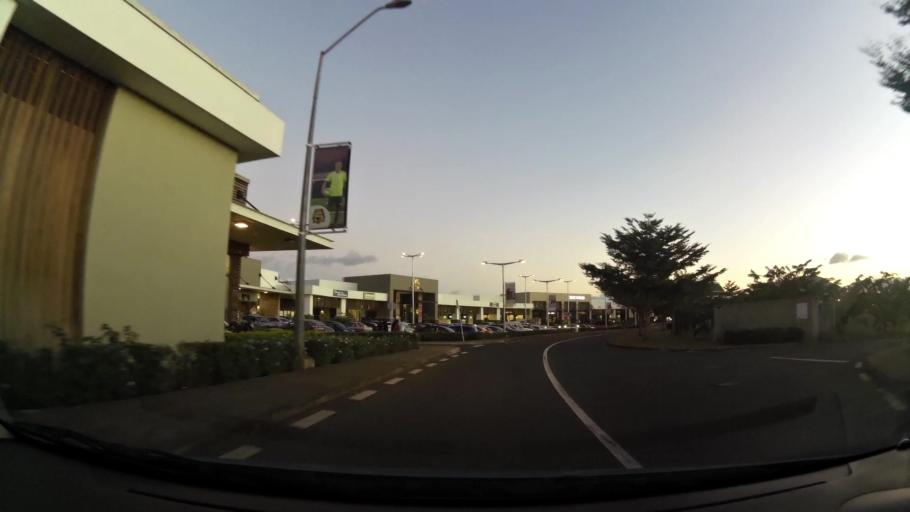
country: MU
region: Moka
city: Moka
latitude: -20.2258
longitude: 57.4987
